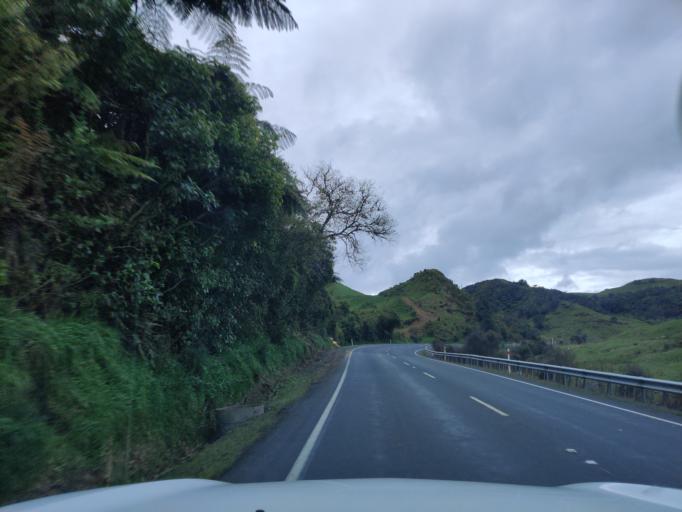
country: NZ
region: Waikato
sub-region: Otorohanga District
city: Otorohanga
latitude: -38.5168
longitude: 175.2073
